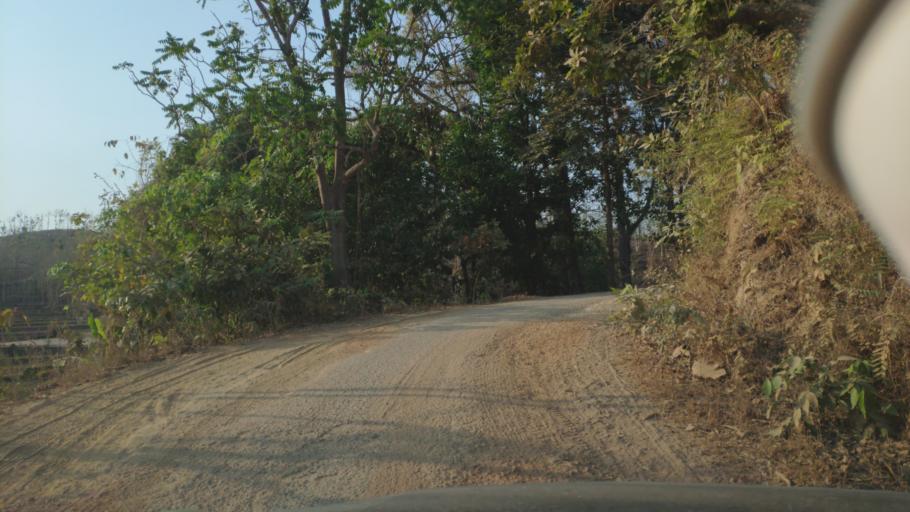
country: ID
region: Central Java
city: Sendangrejo
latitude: -6.9072
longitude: 111.5507
